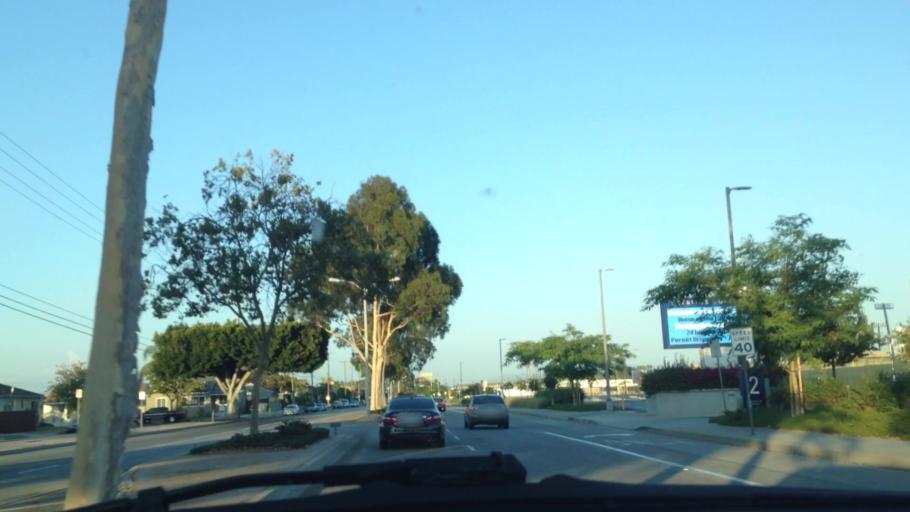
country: US
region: California
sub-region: Los Angeles County
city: Norwalk
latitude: 33.8875
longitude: -118.0951
